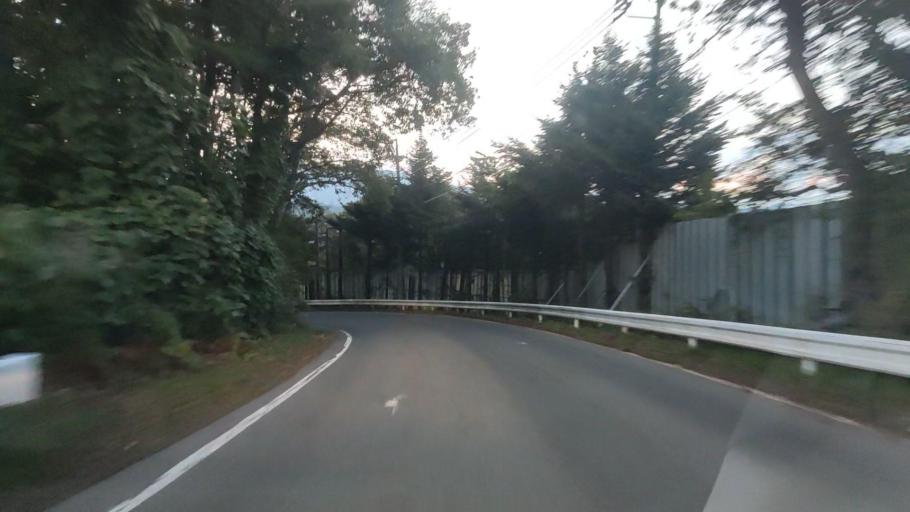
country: JP
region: Gunma
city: Nakanojomachi
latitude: 36.5426
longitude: 138.6055
